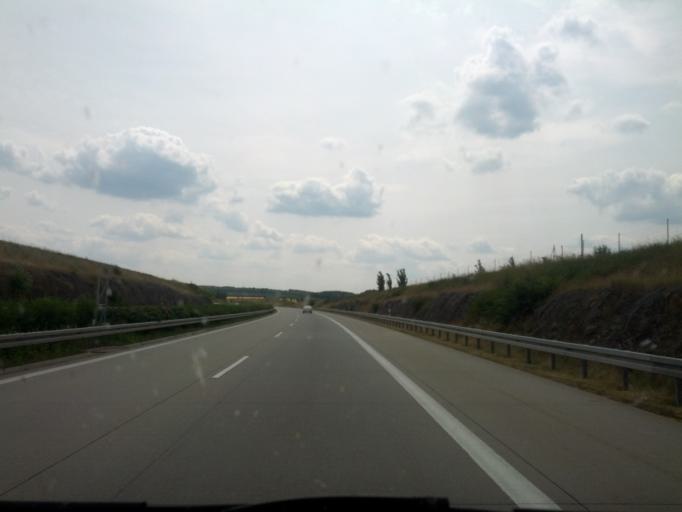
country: DE
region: Saxony
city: Liebstadt
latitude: 50.8122
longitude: 13.8827
